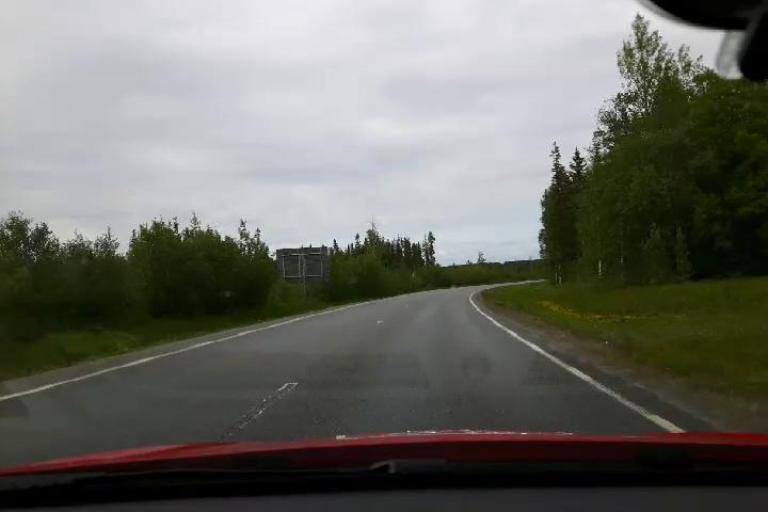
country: SE
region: Jaemtland
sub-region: Bergs Kommun
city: Hoverberg
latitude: 62.9167
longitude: 14.3281
